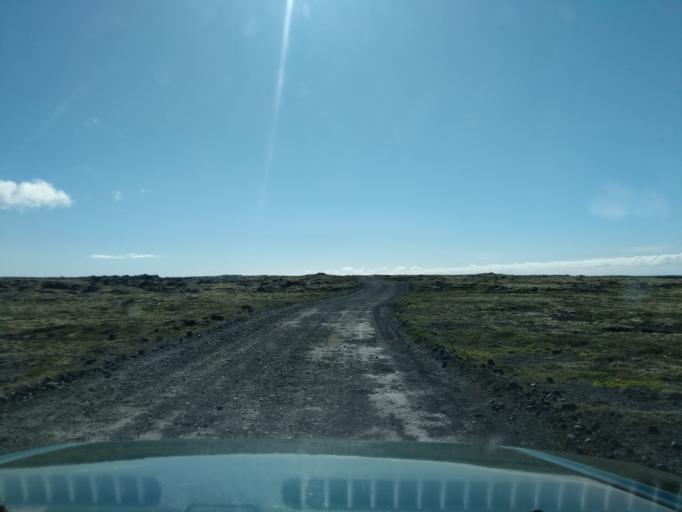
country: IS
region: West
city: Olafsvik
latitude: 64.8723
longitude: -24.0253
